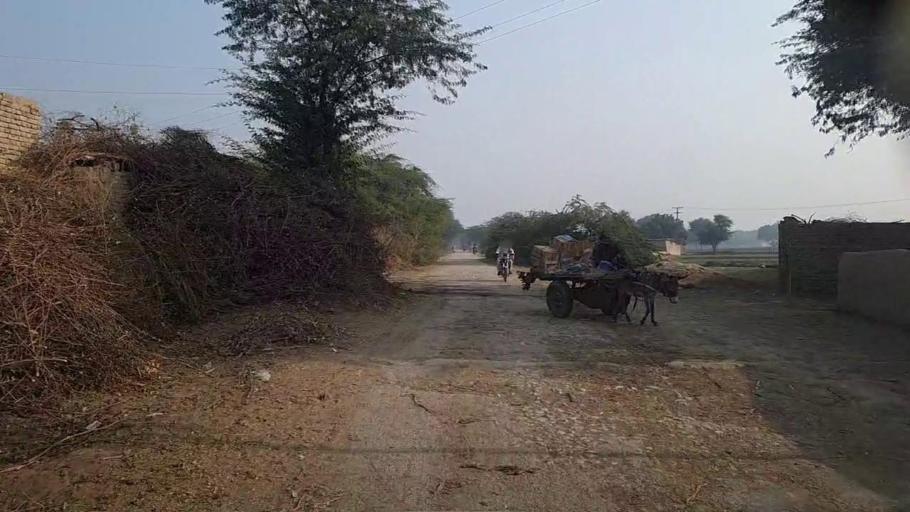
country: PK
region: Sindh
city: Kandiari
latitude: 27.0361
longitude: 68.4818
